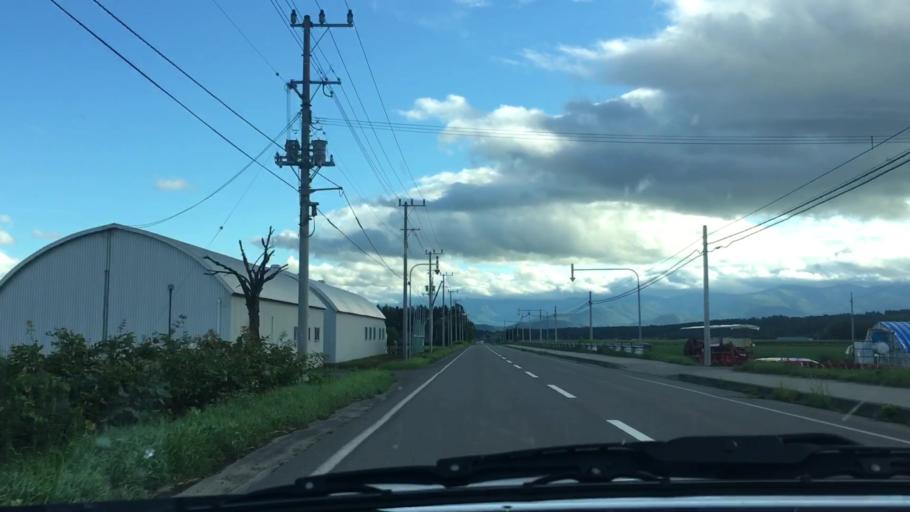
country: JP
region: Hokkaido
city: Otofuke
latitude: 43.1474
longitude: 142.8987
